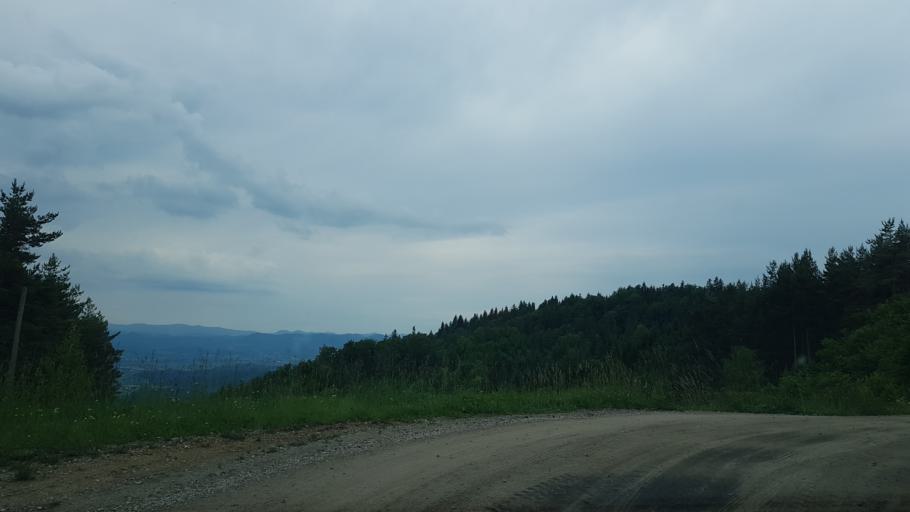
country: SI
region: Dobrna
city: Dobrna
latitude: 46.3659
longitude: 15.2461
